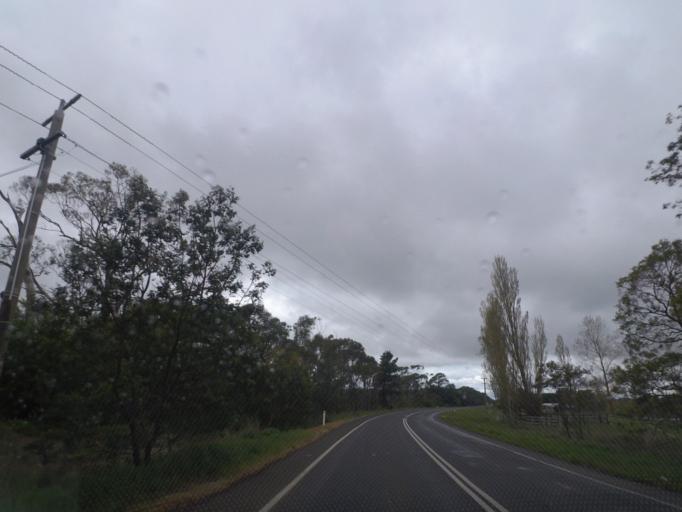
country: AU
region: Victoria
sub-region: Hume
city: Sunbury
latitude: -37.3449
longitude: 144.7003
